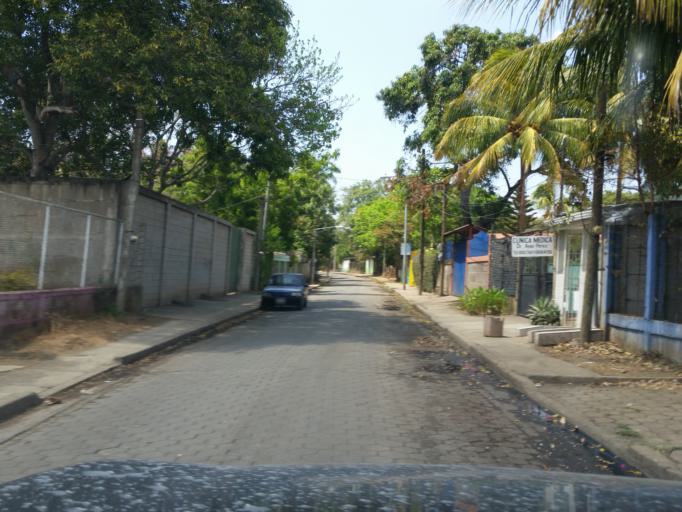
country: NI
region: Masaya
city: Ticuantepe
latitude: 12.0727
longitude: -86.2145
